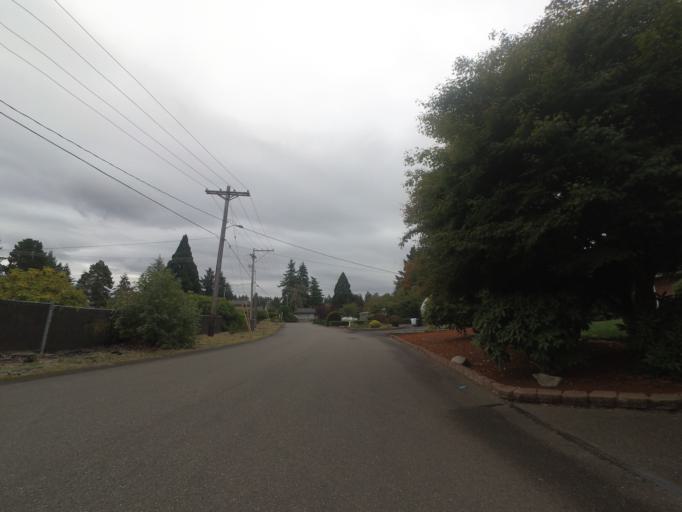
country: US
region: Washington
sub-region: Pierce County
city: Lakewood
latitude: 47.1534
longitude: -122.5117
